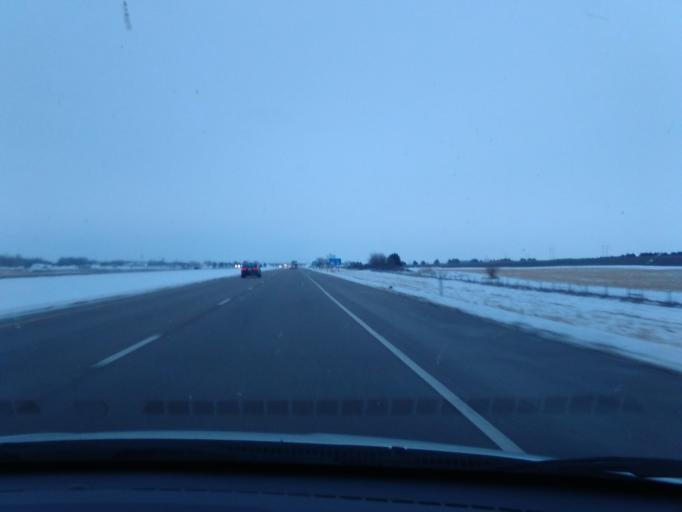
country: US
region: Nebraska
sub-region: Lincoln County
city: Sutherland
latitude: 41.1092
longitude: -101.3710
